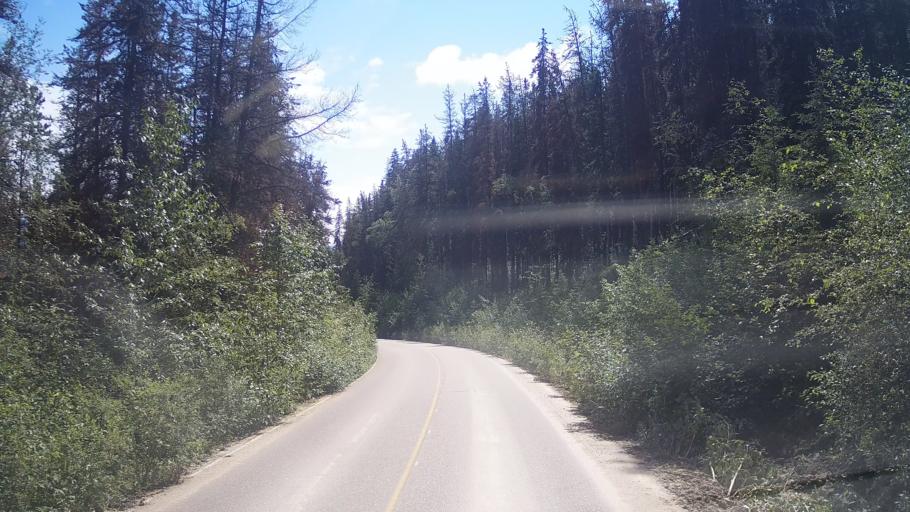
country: CA
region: Alberta
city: Jasper Park Lodge
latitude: 52.7687
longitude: -118.0298
